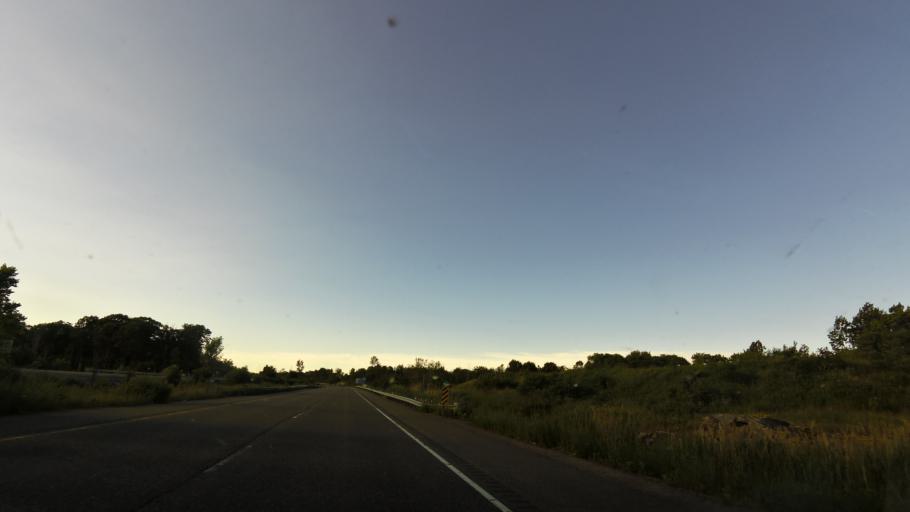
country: CA
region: Ontario
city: Midland
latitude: 44.8253
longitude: -79.7372
